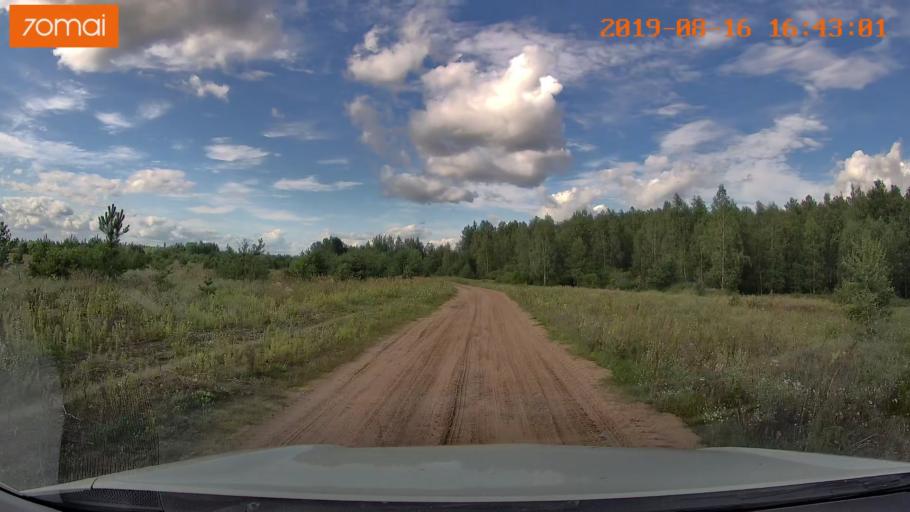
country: BY
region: Mogilev
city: Asipovichy
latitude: 53.2423
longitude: 28.7774
